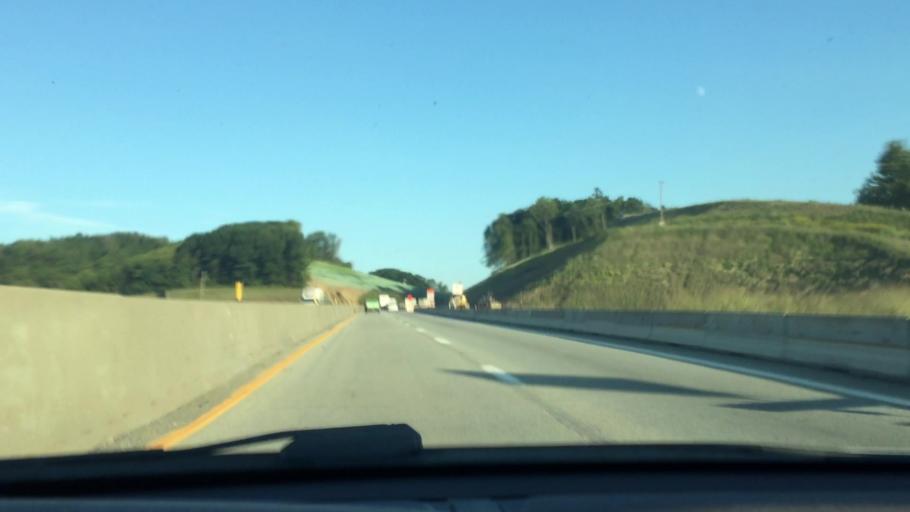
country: US
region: Pennsylvania
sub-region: Washington County
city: East Washington
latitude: 40.1660
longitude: -80.1705
